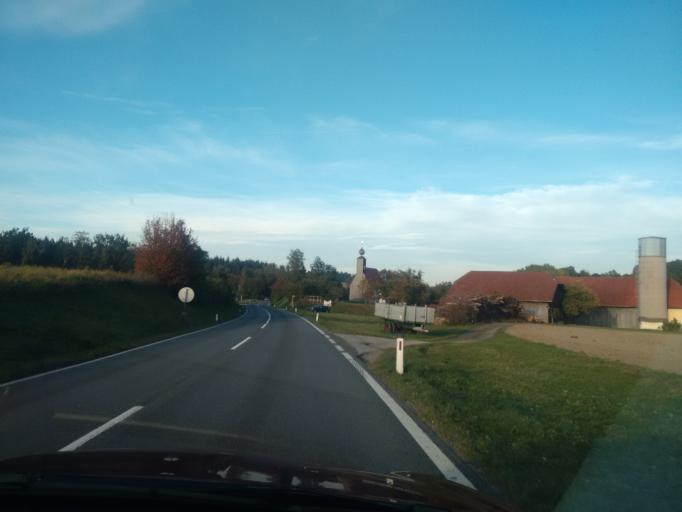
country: AT
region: Upper Austria
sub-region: Politischer Bezirk Vocklabruck
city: Niederthalheim
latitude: 48.1648
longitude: 13.7493
